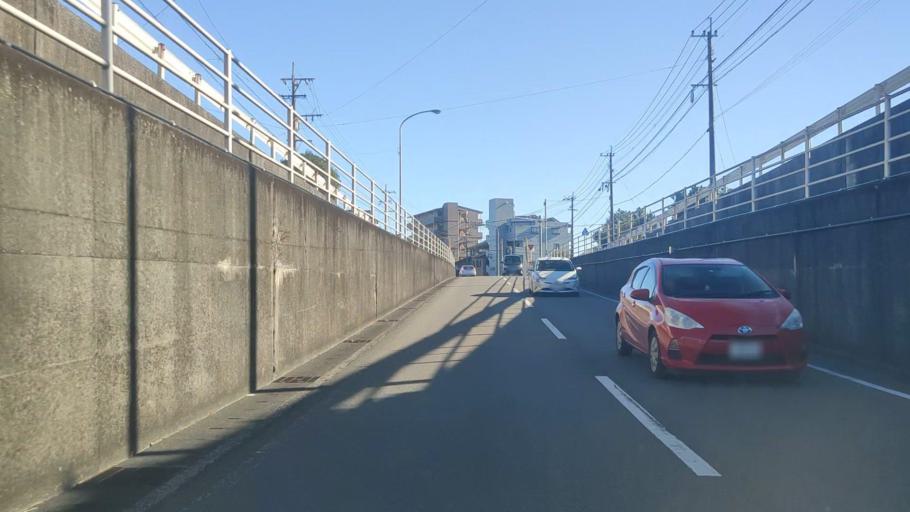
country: JP
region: Miyazaki
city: Miyazaki-shi
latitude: 31.8982
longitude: 131.4262
